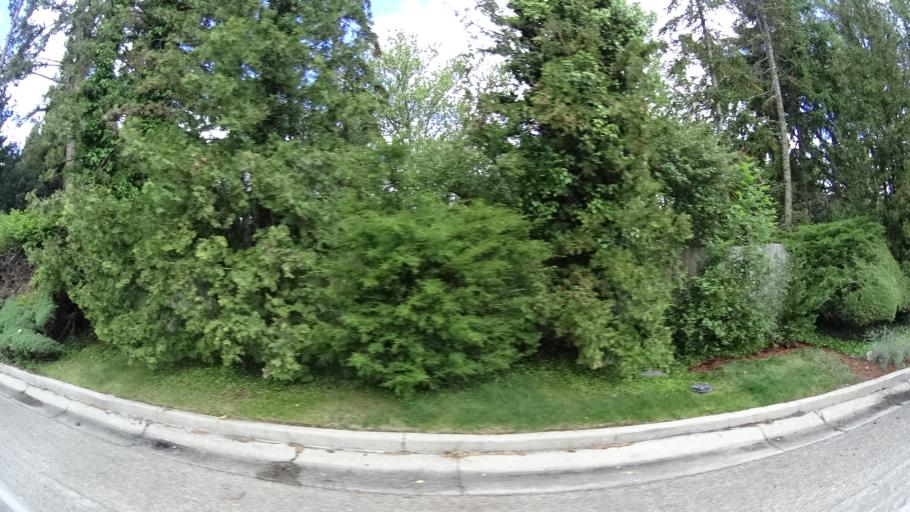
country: US
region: Idaho
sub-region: Ada County
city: Boise
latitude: 43.6456
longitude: -116.1986
